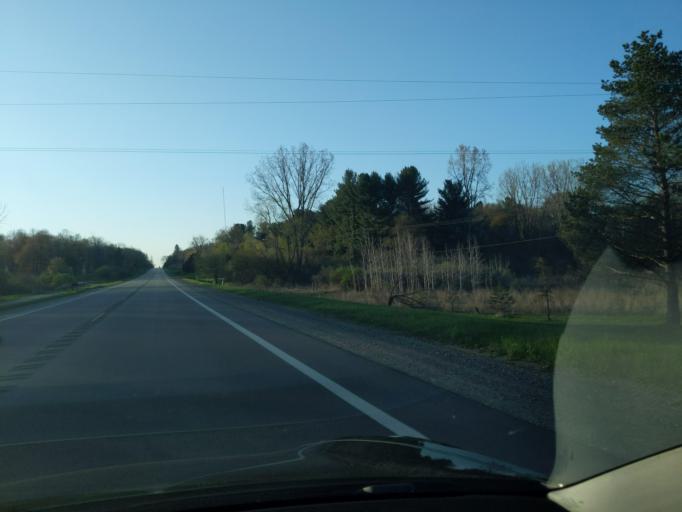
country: US
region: Michigan
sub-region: Washtenaw County
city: Chelsea
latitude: 42.3564
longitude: -84.0576
